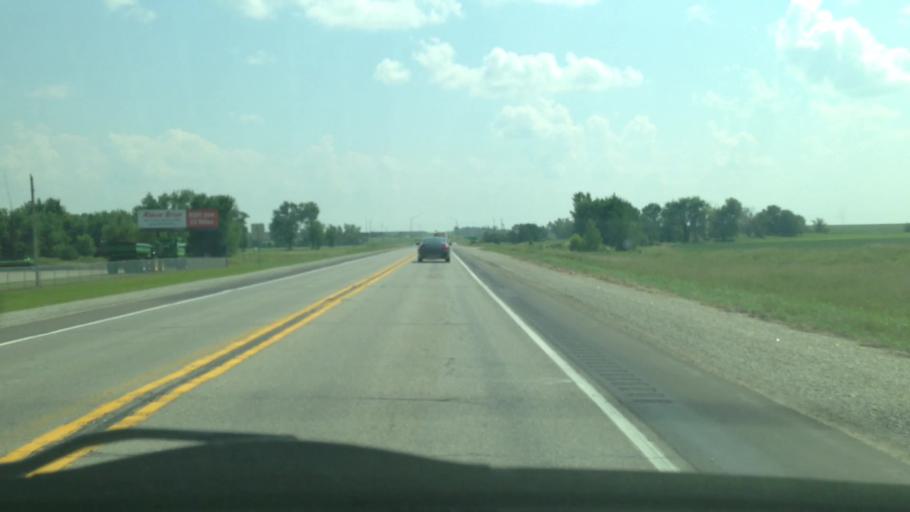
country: US
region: Iowa
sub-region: Howard County
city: Cresco
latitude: 43.3747
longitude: -92.2983
